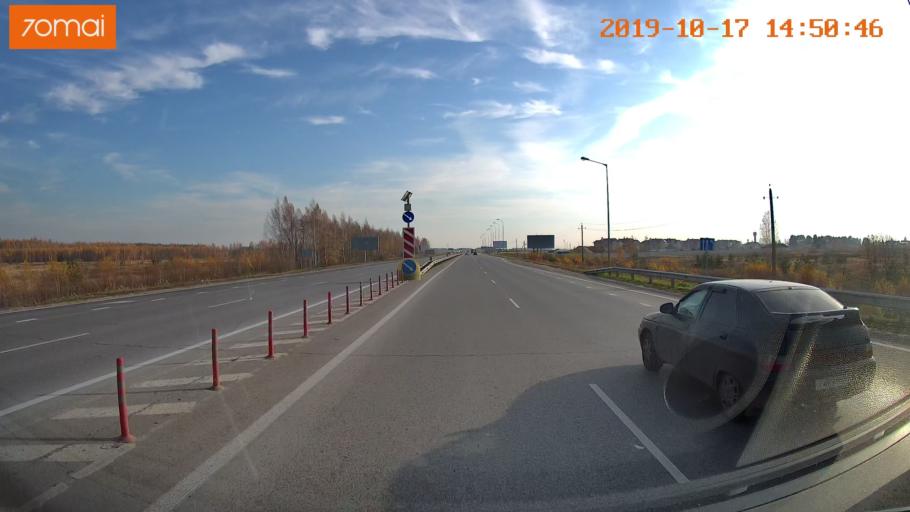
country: RU
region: Rjazan
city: Polyany
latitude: 54.7294
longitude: 39.8444
